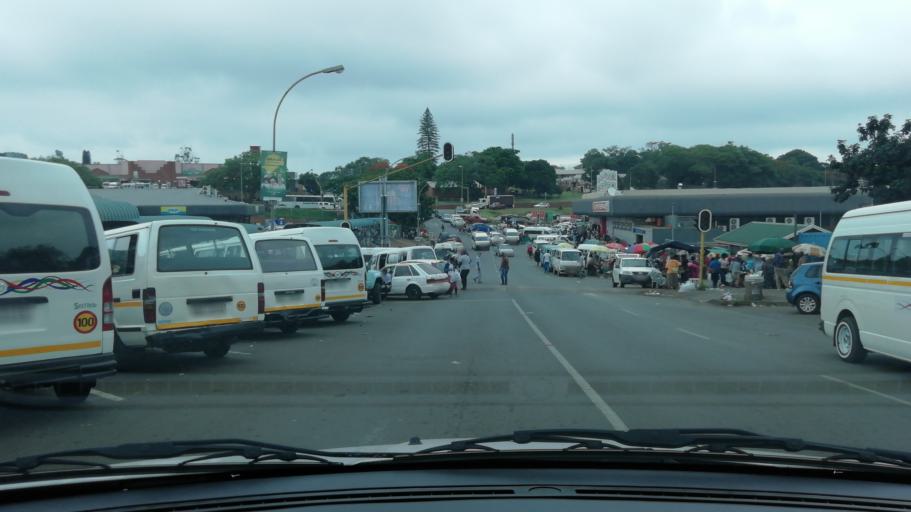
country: ZA
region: KwaZulu-Natal
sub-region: uThungulu District Municipality
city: Empangeni
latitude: -28.7442
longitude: 31.8892
